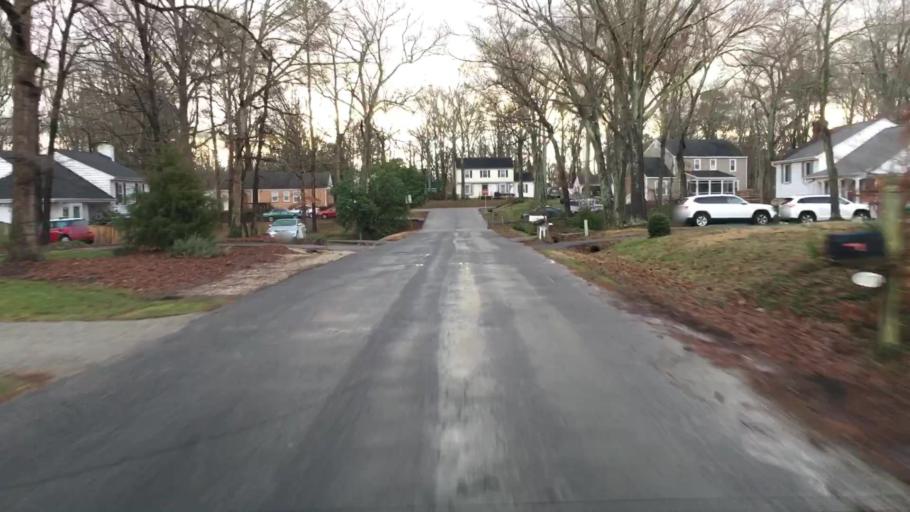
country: US
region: Virginia
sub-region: Chesterfield County
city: Bon Air
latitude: 37.5174
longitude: -77.6213
